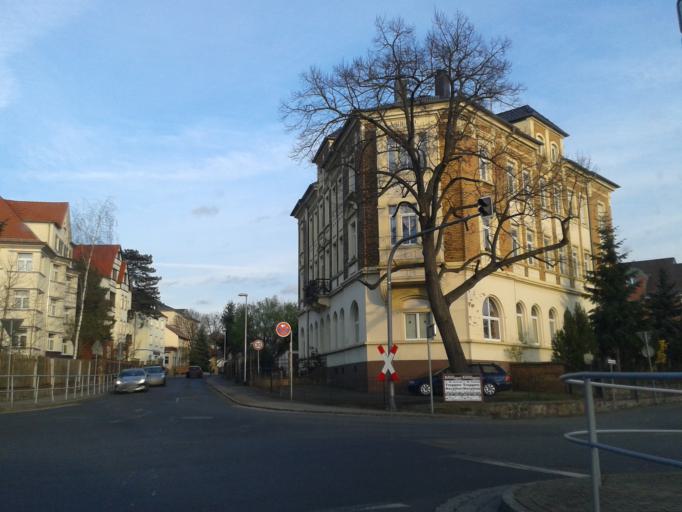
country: DE
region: Saxony
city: Radebeul
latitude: 51.1010
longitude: 13.6747
